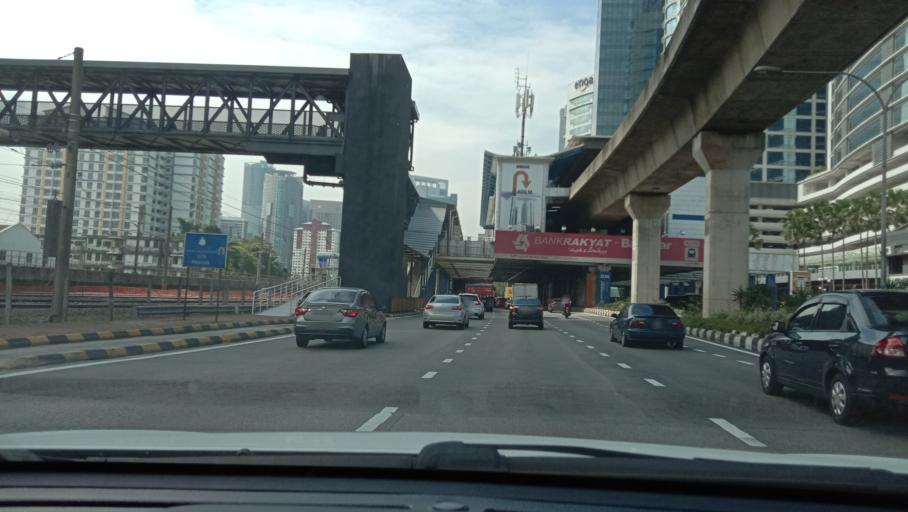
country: MY
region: Kuala Lumpur
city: Kuala Lumpur
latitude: 3.1284
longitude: 101.6798
